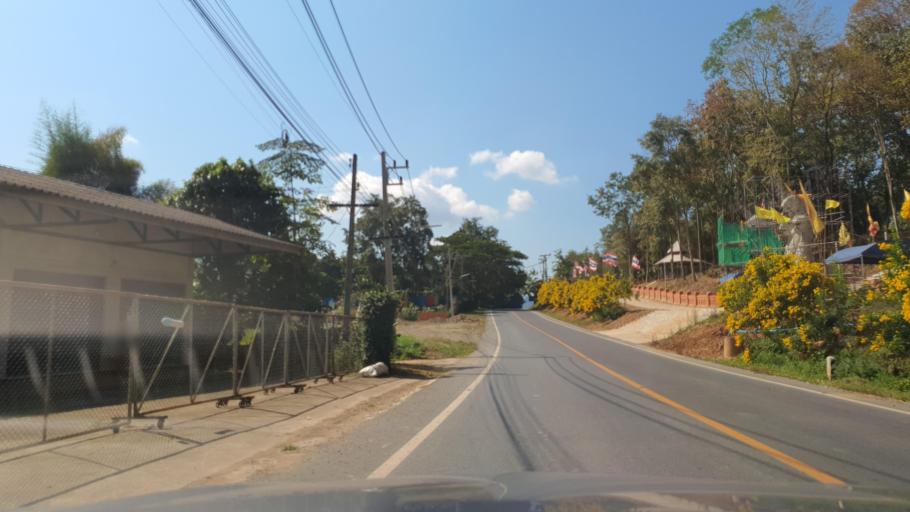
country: TH
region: Nan
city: Tha Wang Pha
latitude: 19.0796
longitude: 100.8735
